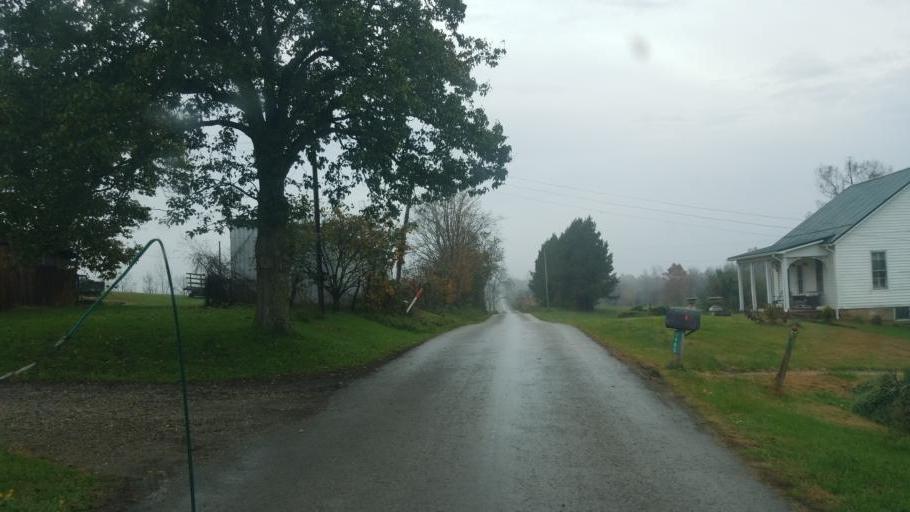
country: US
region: Ohio
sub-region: Morgan County
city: McConnelsville
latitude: 39.5114
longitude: -81.8279
